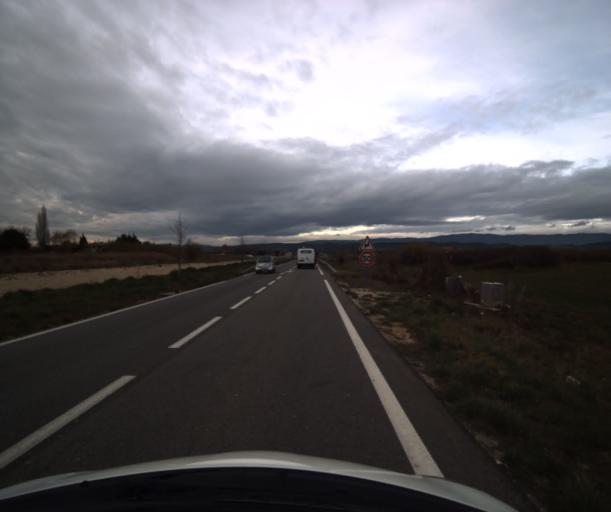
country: FR
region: Provence-Alpes-Cote d'Azur
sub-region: Departement du Vaucluse
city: Pertuis
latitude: 43.6760
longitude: 5.4916
